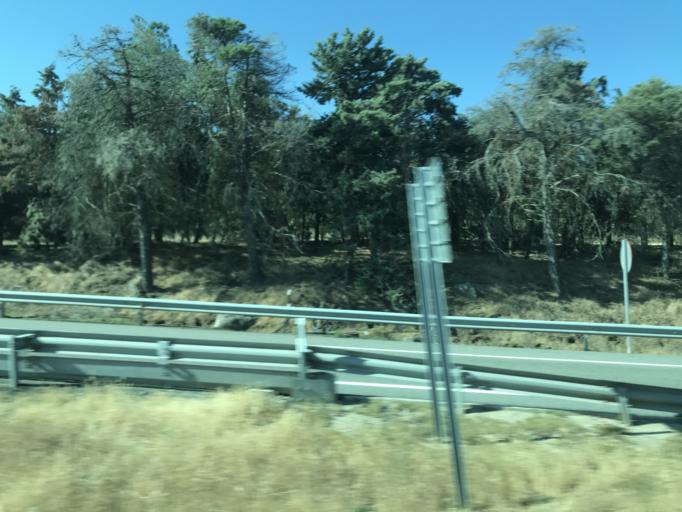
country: ES
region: Castille and Leon
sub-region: Provincia de Segovia
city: Villacastin
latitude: 40.7744
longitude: -4.4220
